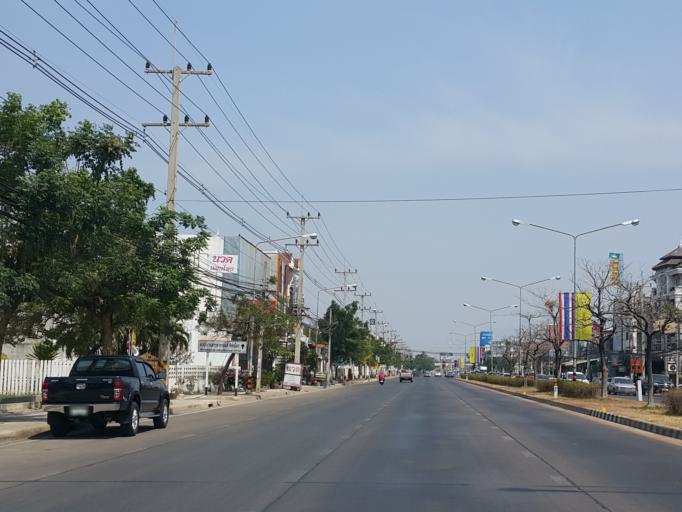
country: TH
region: Phitsanulok
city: Phitsanulok
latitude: 16.8281
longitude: 100.2533
